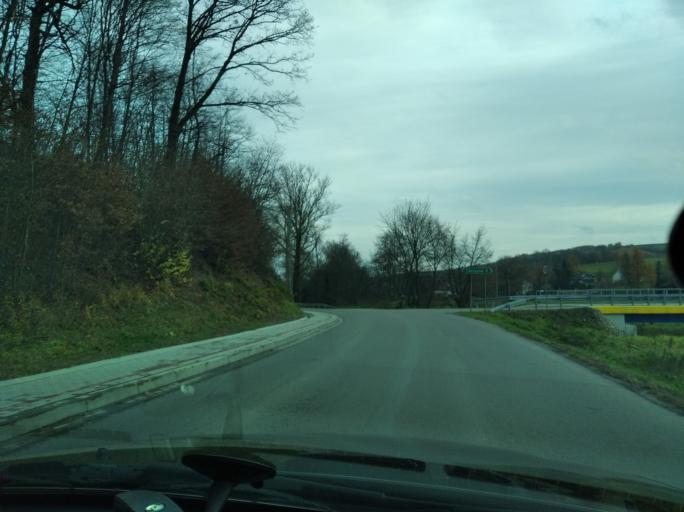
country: PL
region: Subcarpathian Voivodeship
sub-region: Powiat strzyzowski
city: Strzyzow
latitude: 49.9287
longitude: 21.7741
